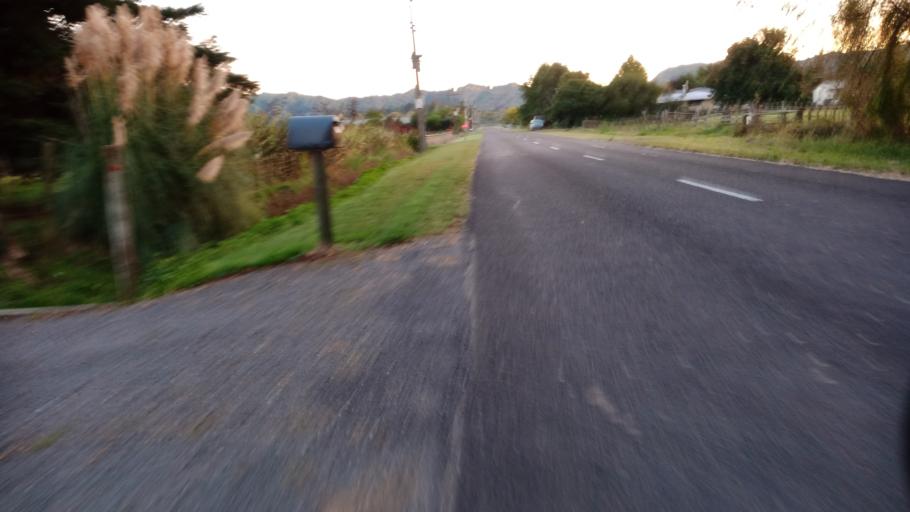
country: NZ
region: Gisborne
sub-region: Gisborne District
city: Gisborne
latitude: -38.6383
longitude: 177.9844
